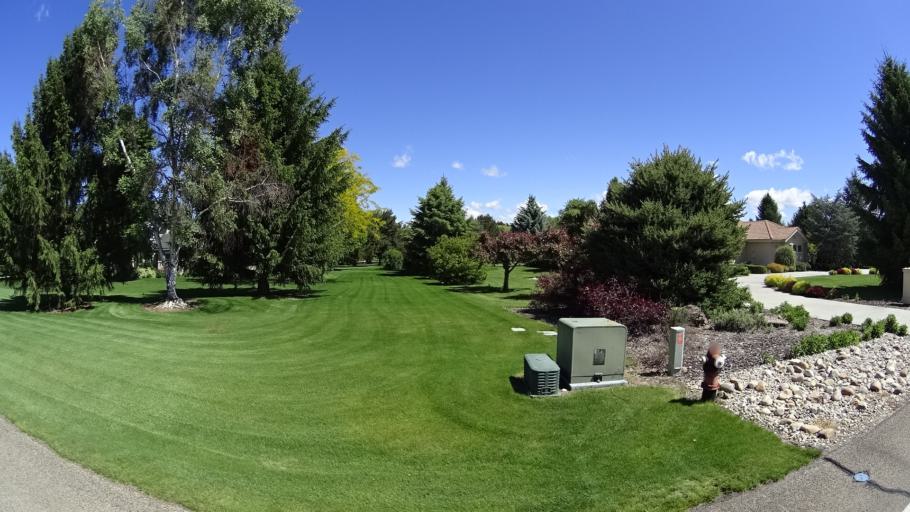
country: US
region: Idaho
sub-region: Ada County
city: Eagle
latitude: 43.6673
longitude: -116.3864
